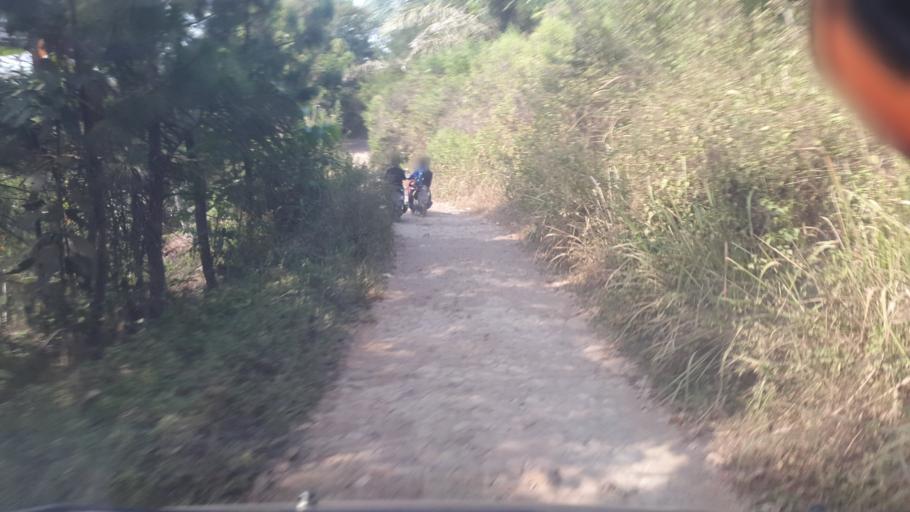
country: ID
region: West Java
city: Ciroyom
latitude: -7.1183
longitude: 106.8352
